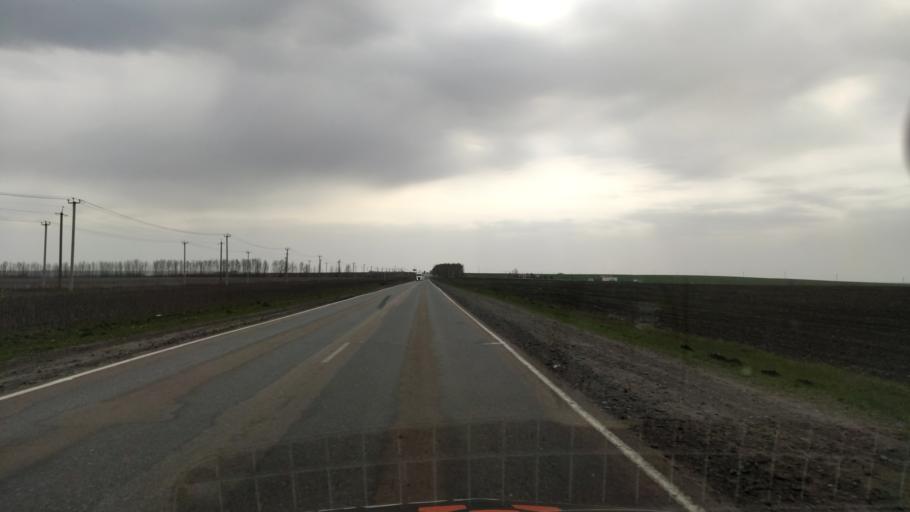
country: RU
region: Kursk
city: Gorshechnoye
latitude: 51.5128
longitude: 38.0058
